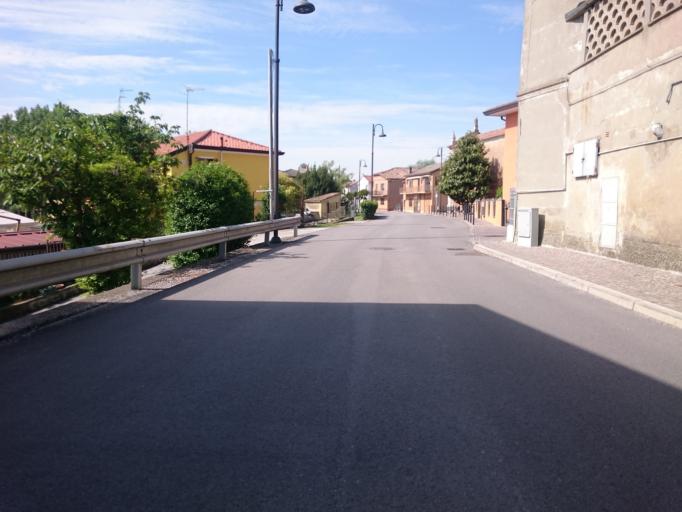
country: IT
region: Veneto
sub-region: Provincia di Rovigo
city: Corbola
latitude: 45.0079
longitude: 12.0791
